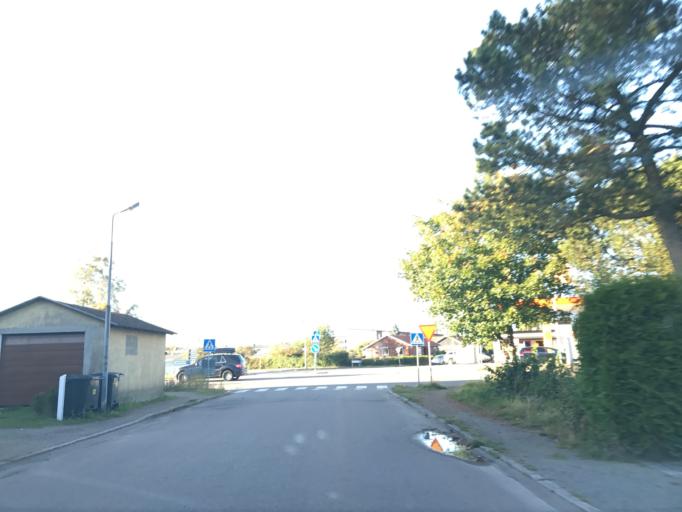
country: SE
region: Skane
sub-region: Klippans Kommun
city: Klippan
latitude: 56.1347
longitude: 13.1491
